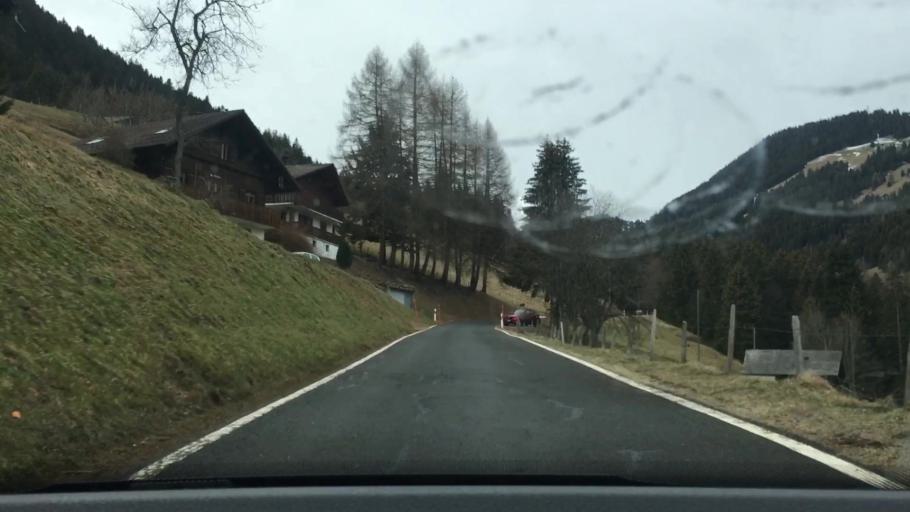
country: CH
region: Valais
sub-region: Monthey District
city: Troistorrents
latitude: 46.2326
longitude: 6.9025
